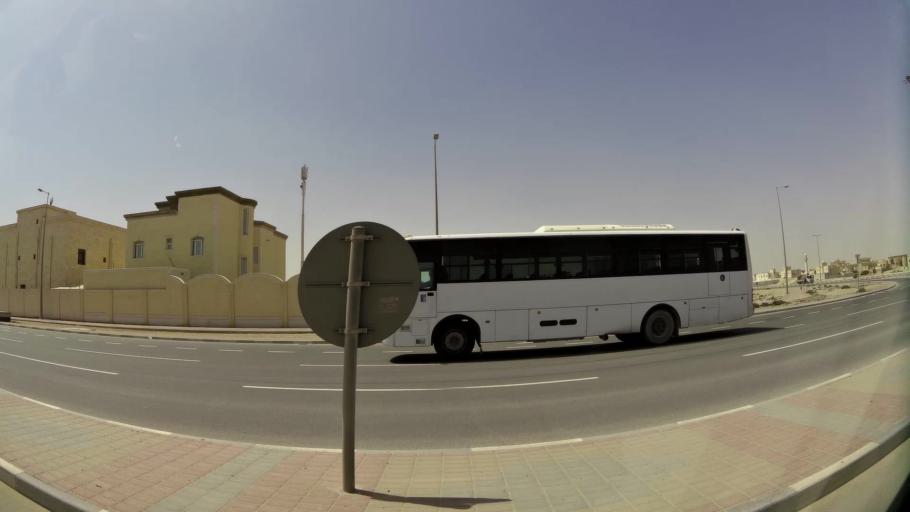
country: QA
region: Baladiyat Umm Salal
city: Umm Salal Muhammad
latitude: 25.4108
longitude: 51.4512
